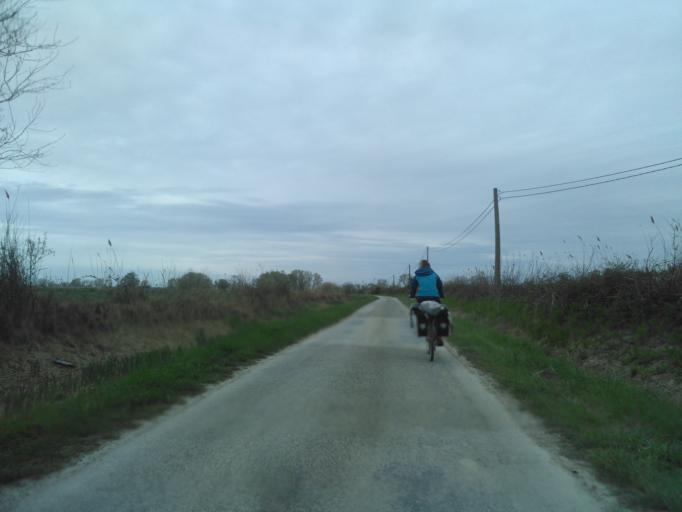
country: FR
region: Provence-Alpes-Cote d'Azur
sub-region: Departement des Bouches-du-Rhone
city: Arles
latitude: 43.5828
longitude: 4.5424
